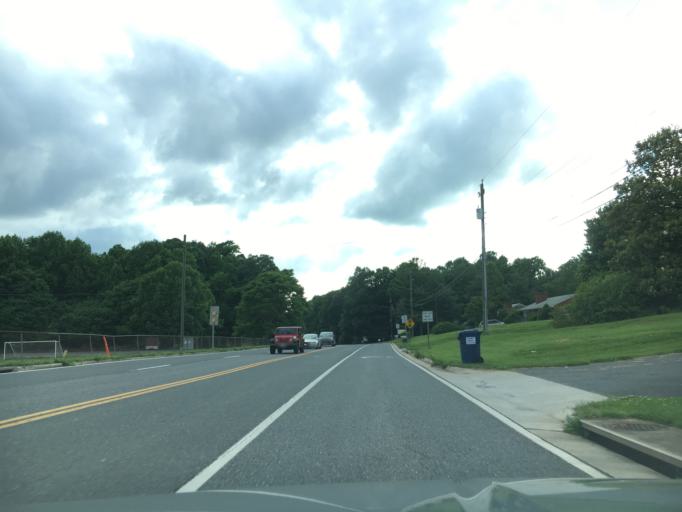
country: US
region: Virginia
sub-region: Campbell County
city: Timberlake
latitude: 37.3474
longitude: -79.2391
